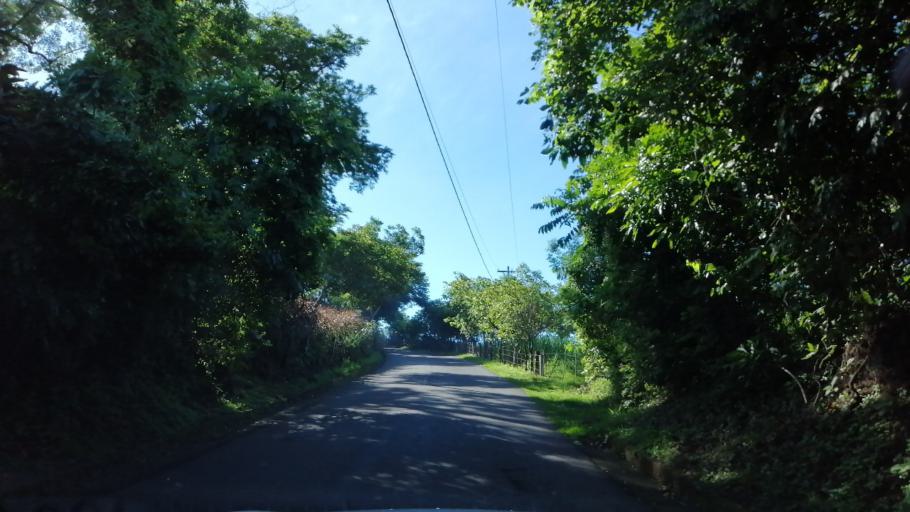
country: SV
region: Morazan
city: Corinto
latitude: 13.7905
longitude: -88.0240
